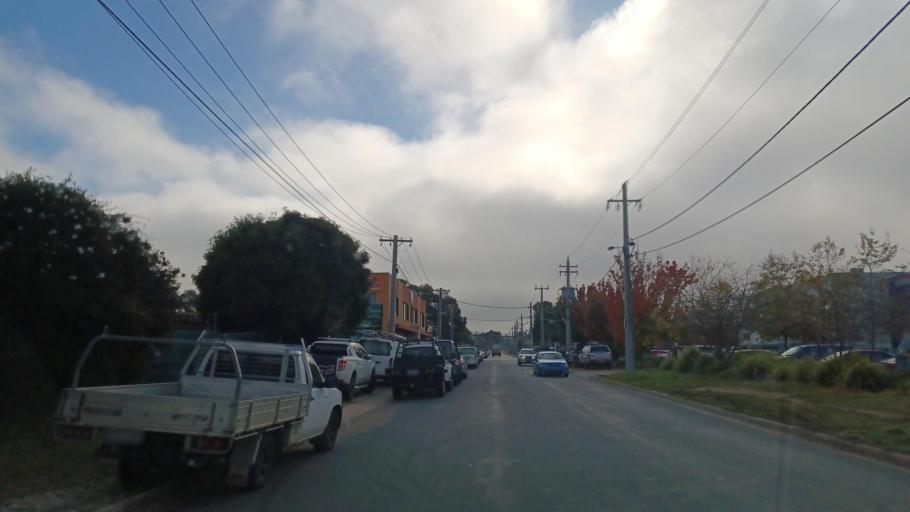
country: AU
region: Australian Capital Territory
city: Kaleen
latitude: -35.2197
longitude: 149.1436
